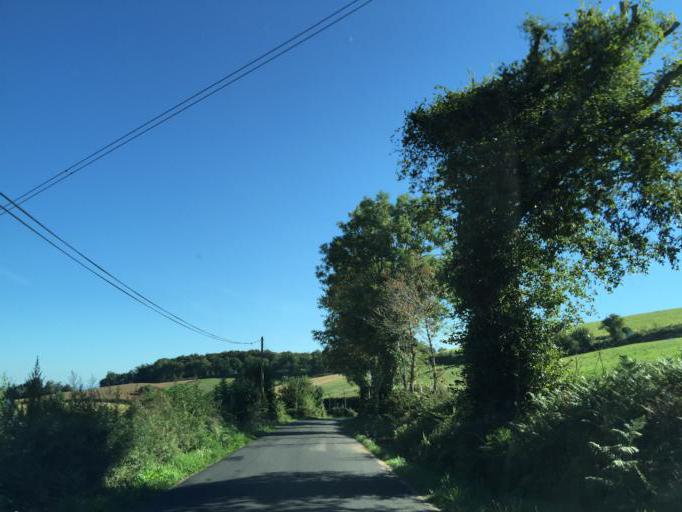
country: FR
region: Midi-Pyrenees
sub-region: Departement de l'Aveyron
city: Laissac
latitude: 44.3400
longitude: 2.7729
